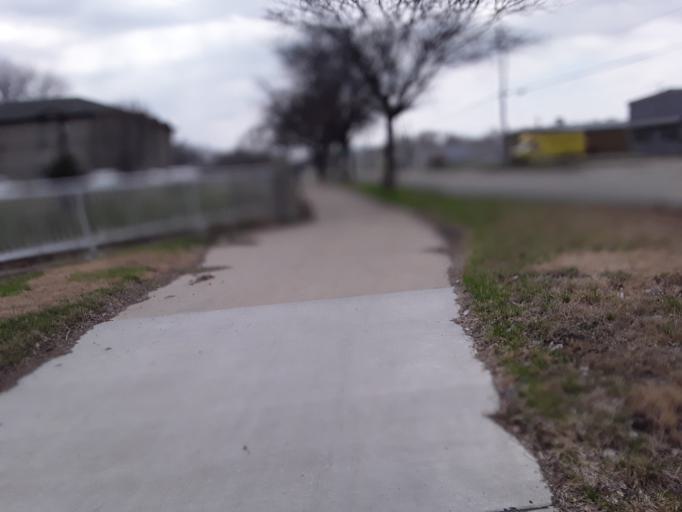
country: US
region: Nebraska
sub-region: Lancaster County
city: Lincoln
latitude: 40.8383
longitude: -96.6727
